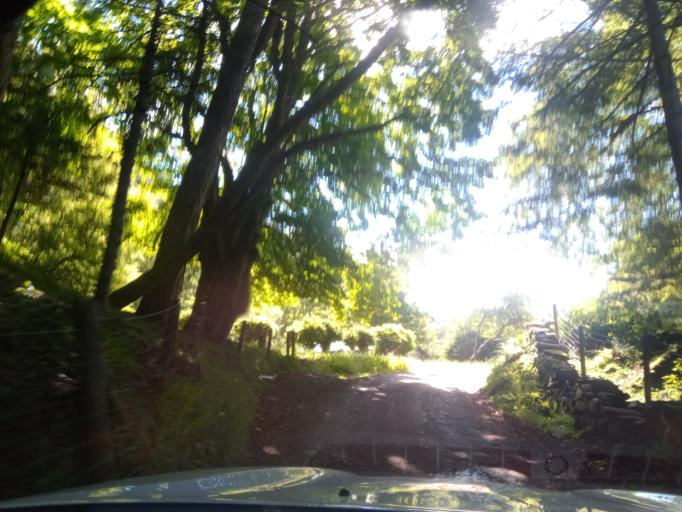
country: GB
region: Scotland
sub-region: Argyll and Bute
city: Isle Of Mull
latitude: 56.7801
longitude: -5.8255
